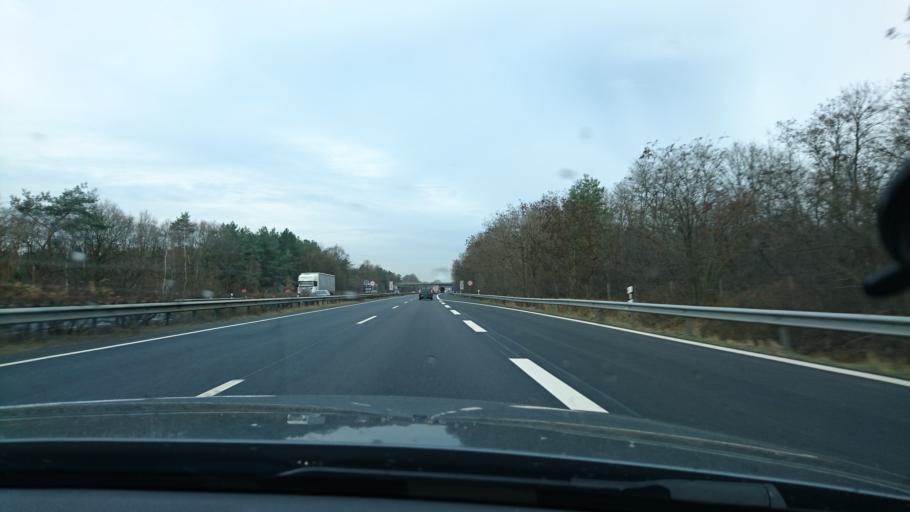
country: DE
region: Lower Saxony
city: Holdorf
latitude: 52.5775
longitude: 8.1099
